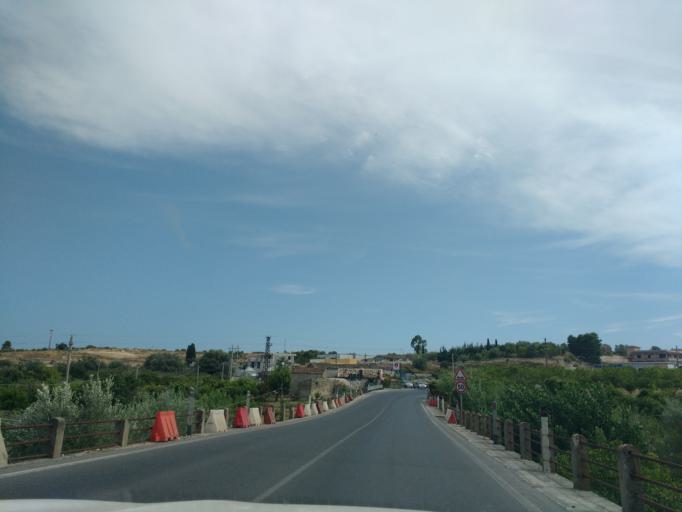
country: IT
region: Sicily
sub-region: Provincia di Siracusa
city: Noto
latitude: 36.8836
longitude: 15.0631
